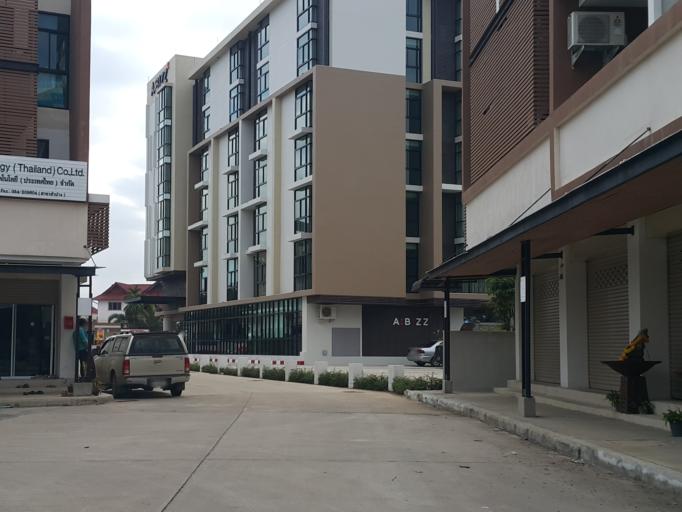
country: TH
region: Lampang
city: Lampang
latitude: 18.2758
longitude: 99.4980
